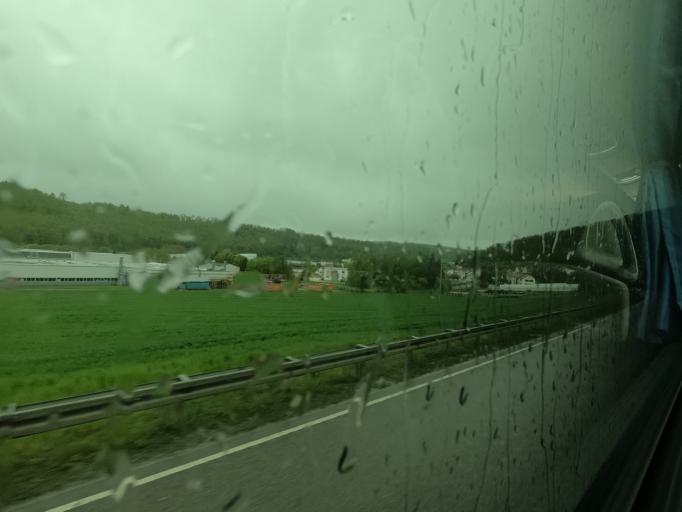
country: DE
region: Baden-Wuerttemberg
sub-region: Regierungsbezirk Stuttgart
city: Konigsbronn
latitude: 48.7382
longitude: 10.1288
